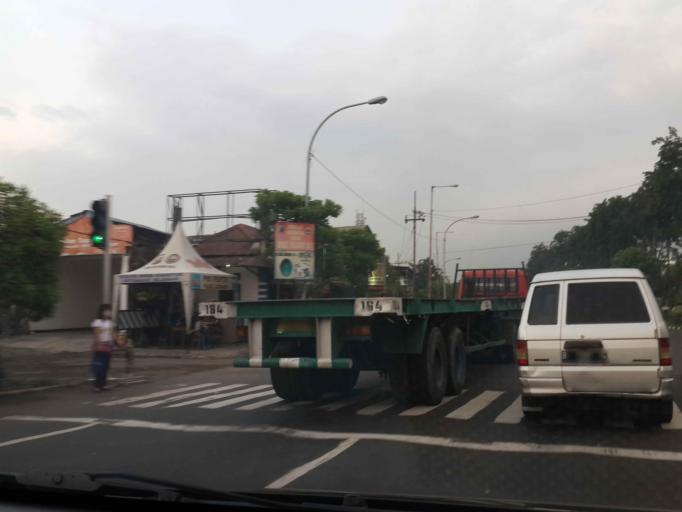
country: ID
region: East Java
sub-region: Kota Surabaya
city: Surabaya
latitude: -7.2448
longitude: 112.7142
